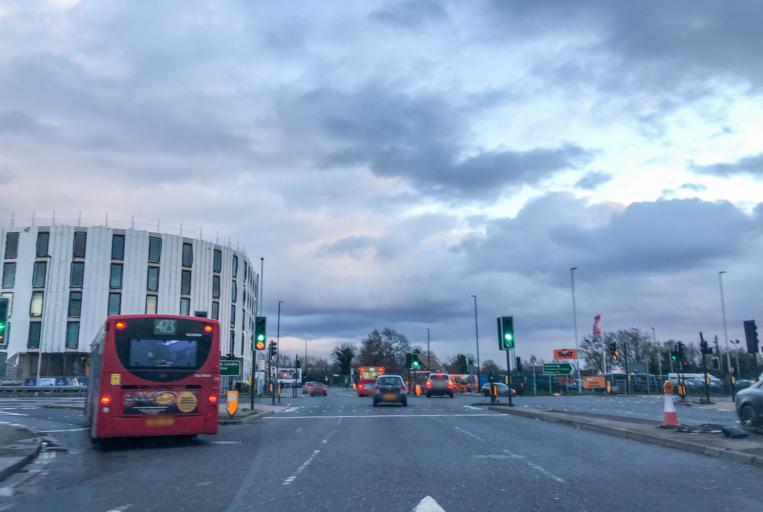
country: GB
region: England
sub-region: Greater London
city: Feltham
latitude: 51.4673
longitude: -0.4225
